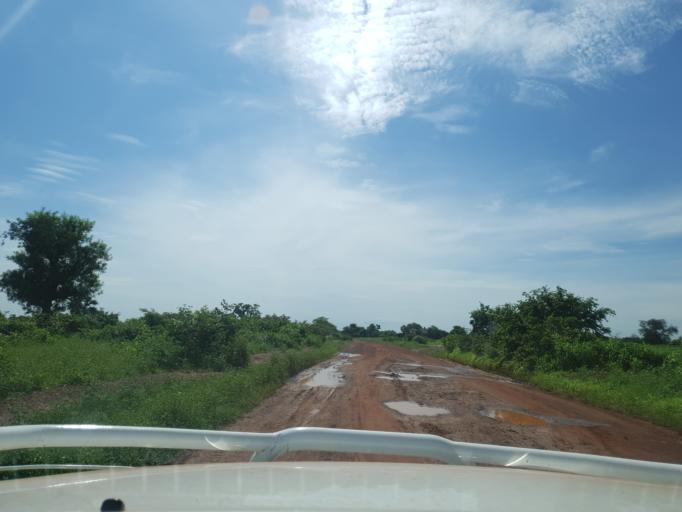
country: ML
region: Koulikoro
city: Banamba
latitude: 13.2752
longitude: -7.5442
